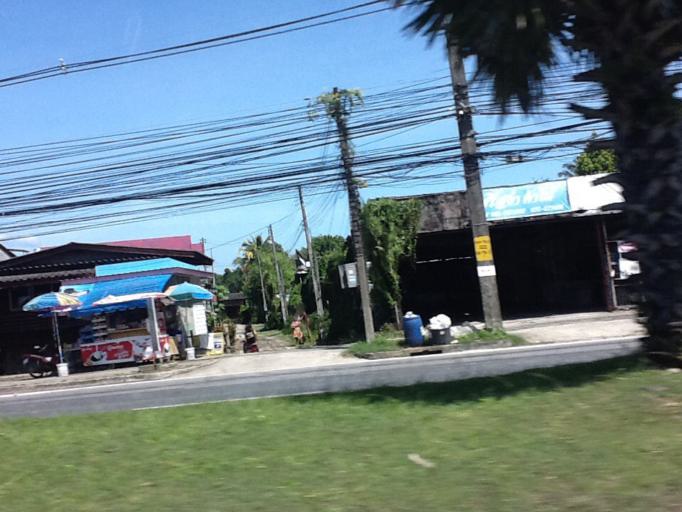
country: TH
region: Phuket
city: Ban Ko Kaeo
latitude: 7.9659
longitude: 98.3748
